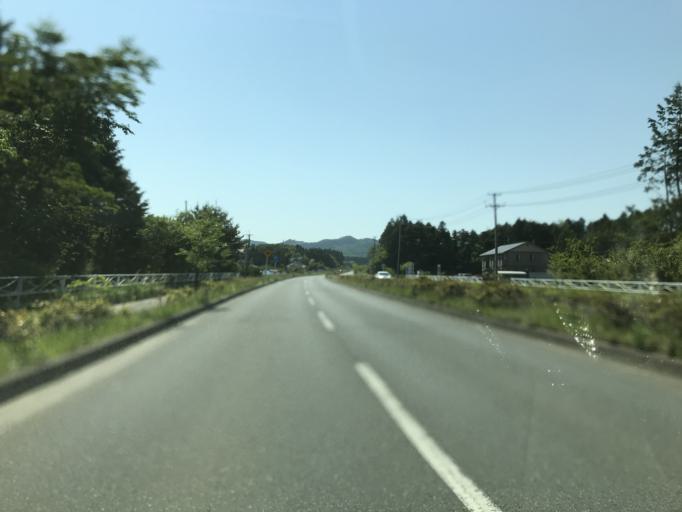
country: JP
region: Miyagi
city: Marumori
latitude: 37.8415
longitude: 140.9043
